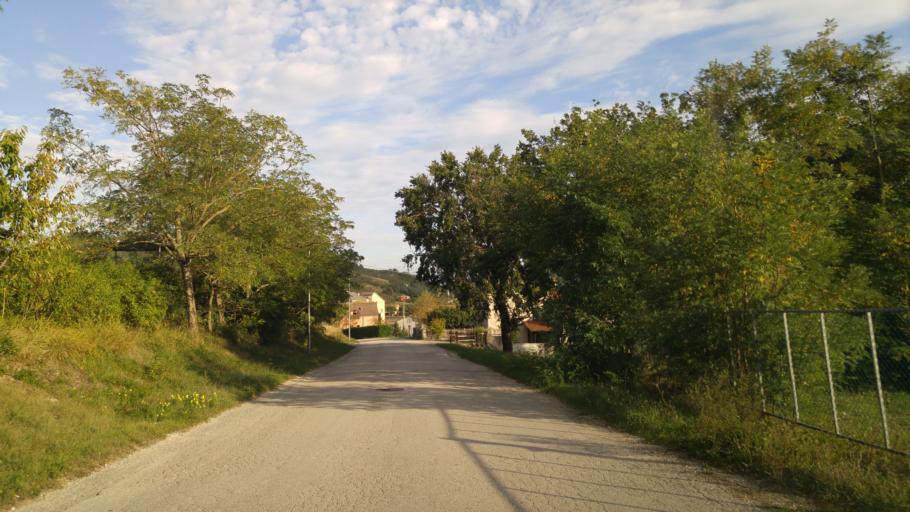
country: IT
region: The Marches
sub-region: Provincia di Pesaro e Urbino
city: Cagli
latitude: 43.5536
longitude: 12.6475
